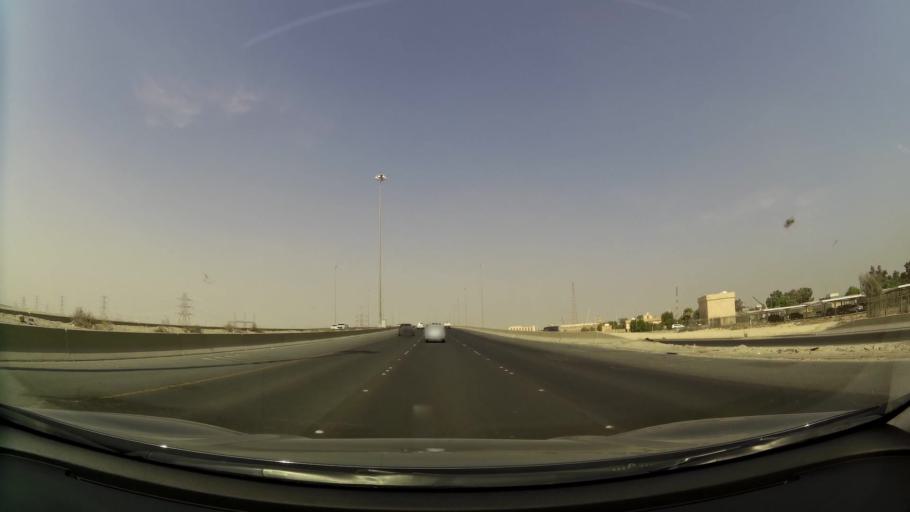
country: KW
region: Al Ahmadi
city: Al Fahahil
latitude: 29.0336
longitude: 48.1205
